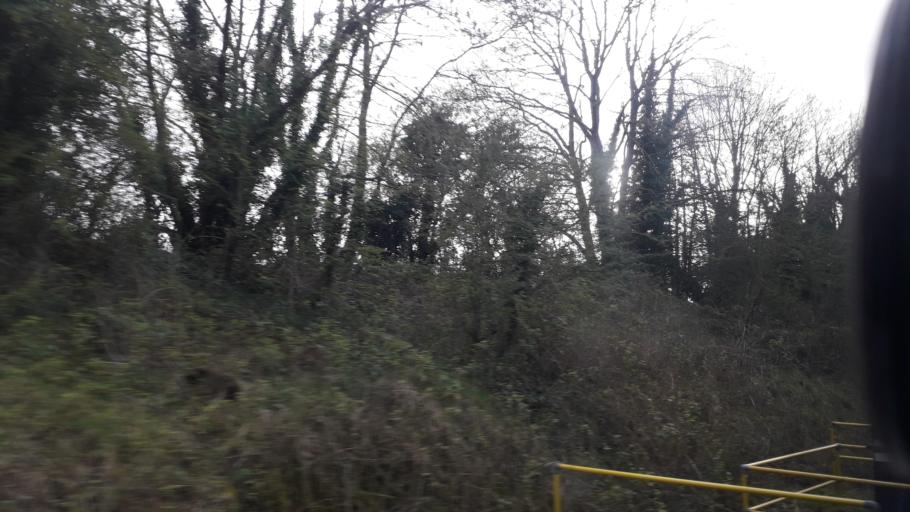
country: IE
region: Leinster
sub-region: An Mhi
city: Enfield
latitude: 53.4124
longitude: -6.8455
